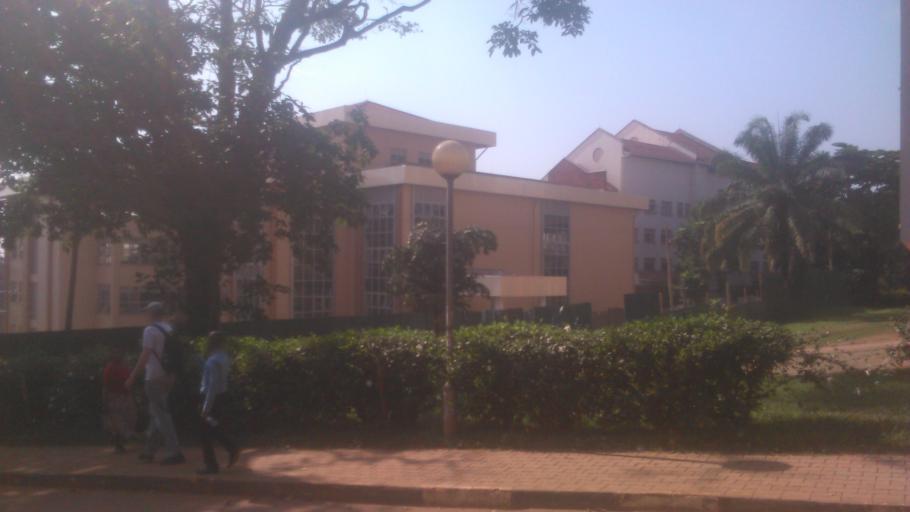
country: UG
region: Central Region
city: Kampala Central Division
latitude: 0.3357
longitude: 32.5676
